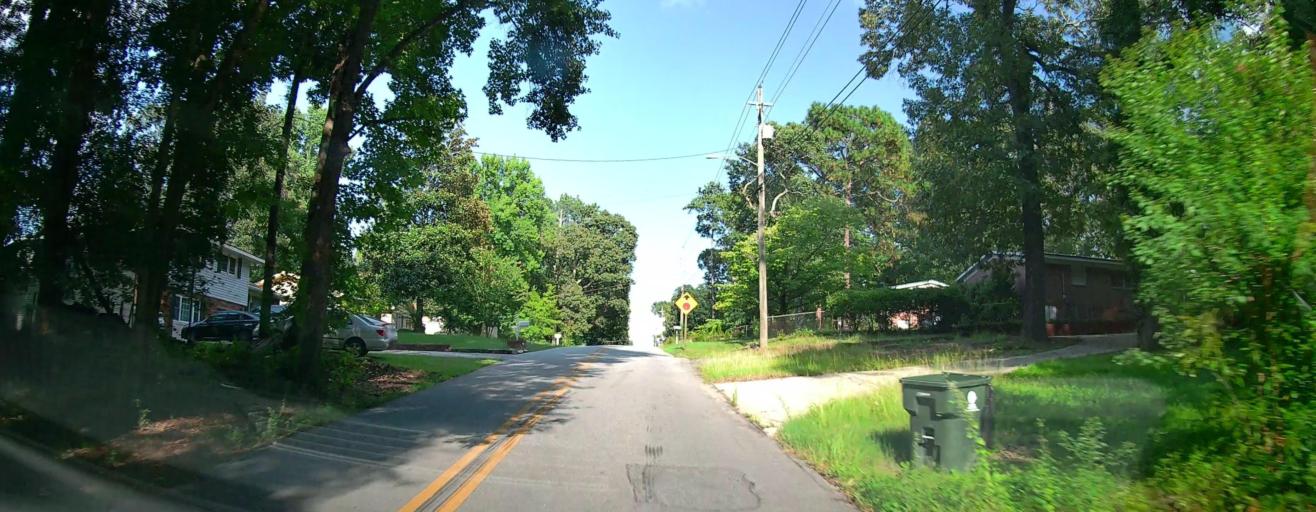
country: US
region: Georgia
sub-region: Houston County
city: Centerville
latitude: 32.5994
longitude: -83.6488
